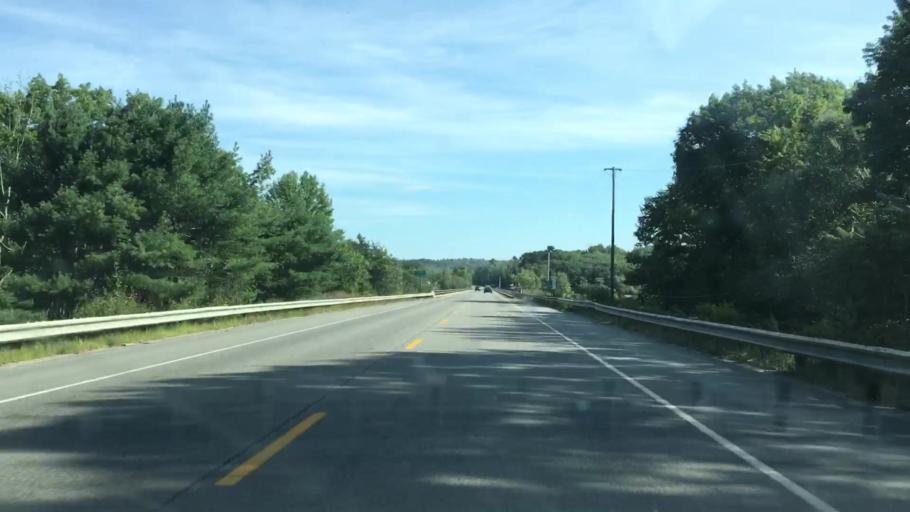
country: US
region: Maine
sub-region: Penobscot County
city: Lincoln
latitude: 45.3645
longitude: -68.5499
